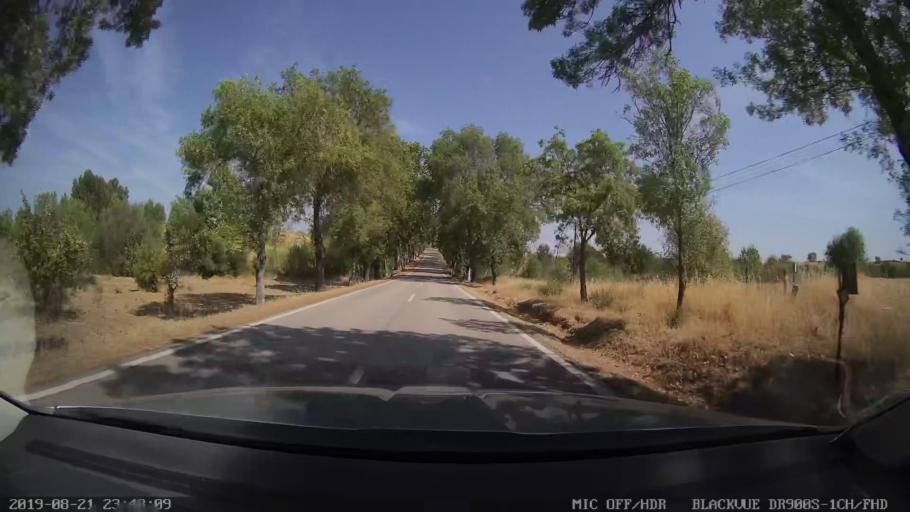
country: PT
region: Castelo Branco
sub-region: Idanha-A-Nova
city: Idanha-a-Nova
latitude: 39.8608
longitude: -7.2586
